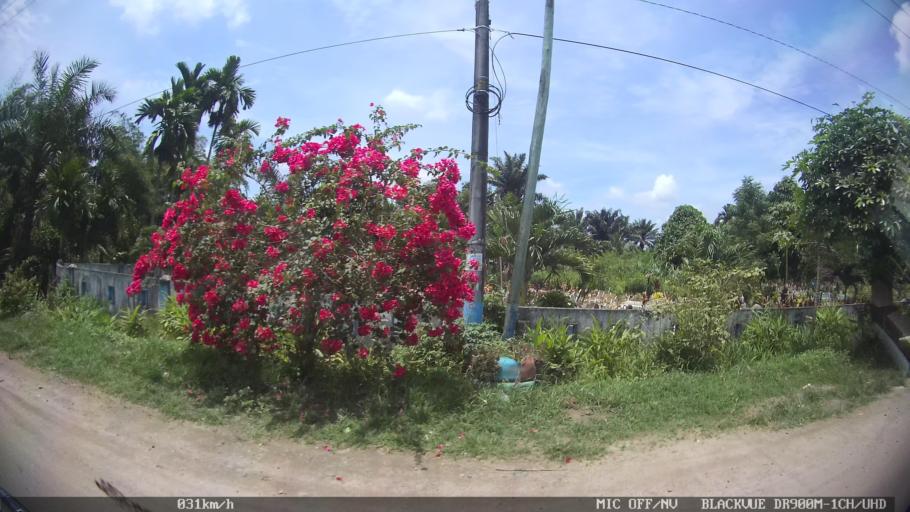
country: ID
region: North Sumatra
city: Perbaungan
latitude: 3.5372
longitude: 98.8827
